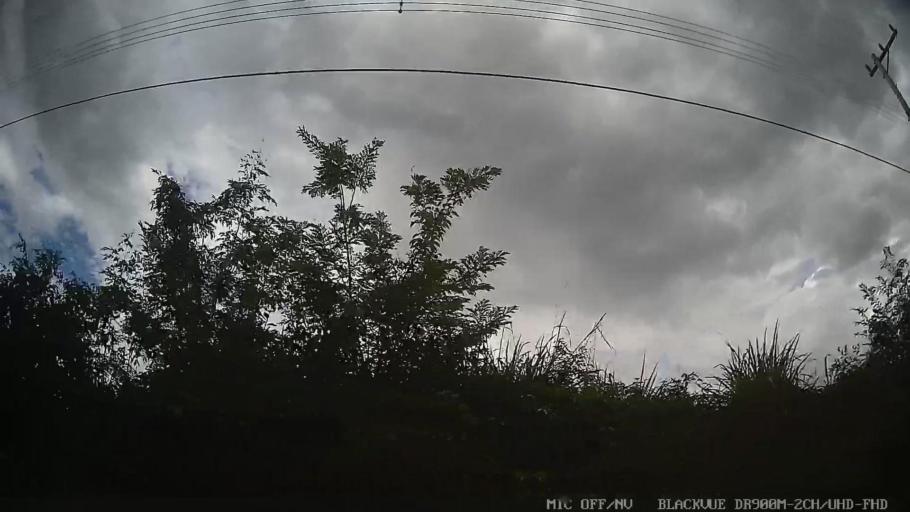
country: BR
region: Sao Paulo
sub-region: Jaguariuna
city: Jaguariuna
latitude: -22.6588
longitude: -46.9820
